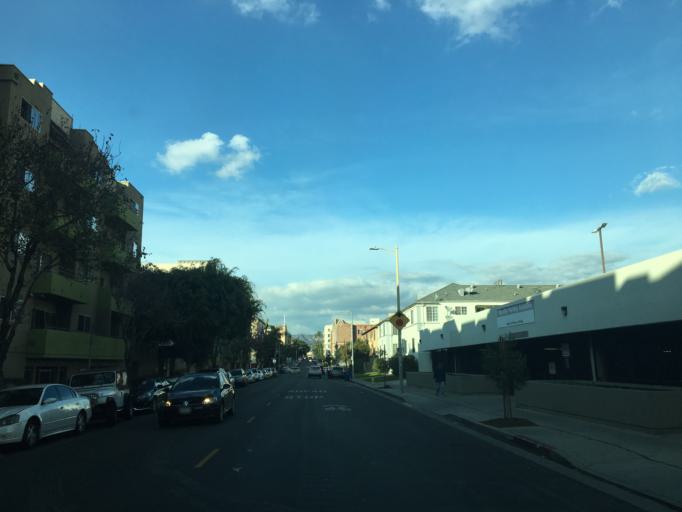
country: US
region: California
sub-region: Los Angeles County
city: Silver Lake
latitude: 34.0643
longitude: -118.2929
